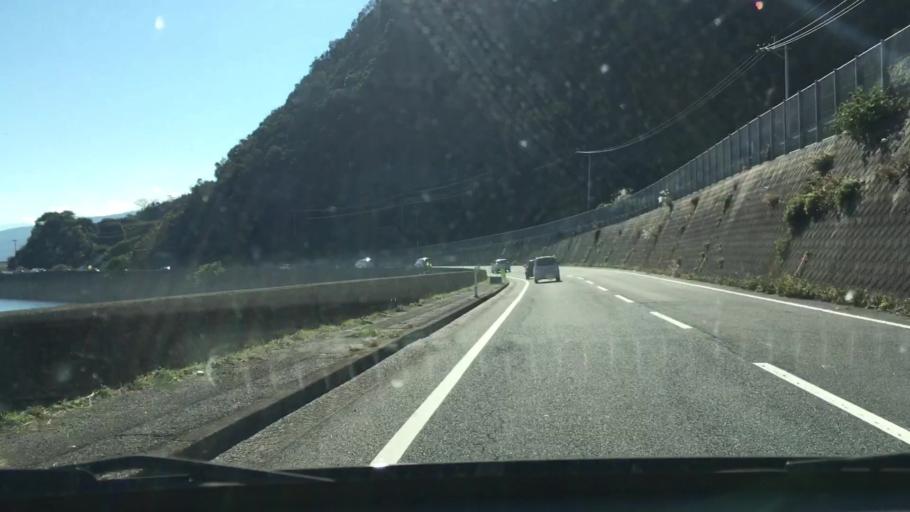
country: JP
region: Kagoshima
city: Kajiki
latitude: 31.6617
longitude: 130.6154
